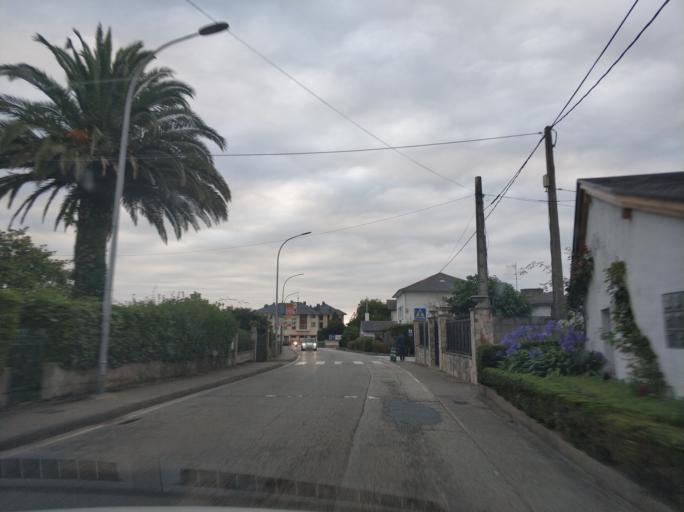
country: ES
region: Asturias
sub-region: Province of Asturias
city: Navia
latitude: 43.5445
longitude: -6.5280
